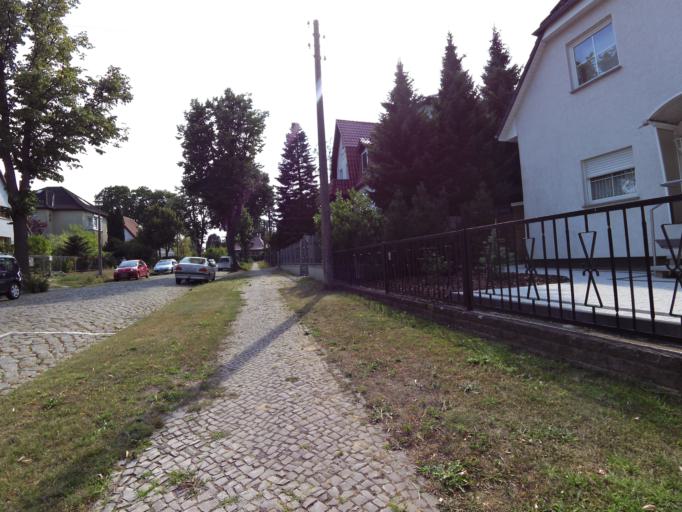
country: DE
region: Berlin
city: Grunau
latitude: 52.4121
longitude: 13.5594
